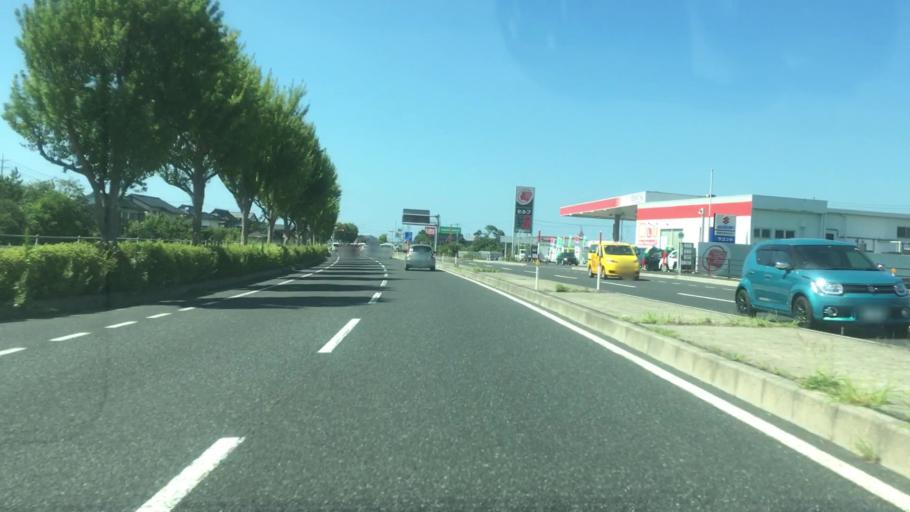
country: JP
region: Tottori
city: Tottori
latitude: 35.4717
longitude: 134.2173
